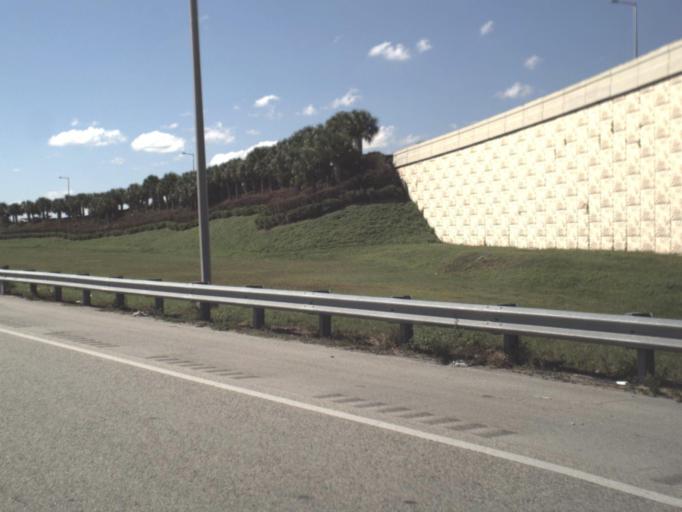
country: US
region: Florida
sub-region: Miami-Dade County
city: Sweetwater
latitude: 25.7758
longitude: -80.3861
